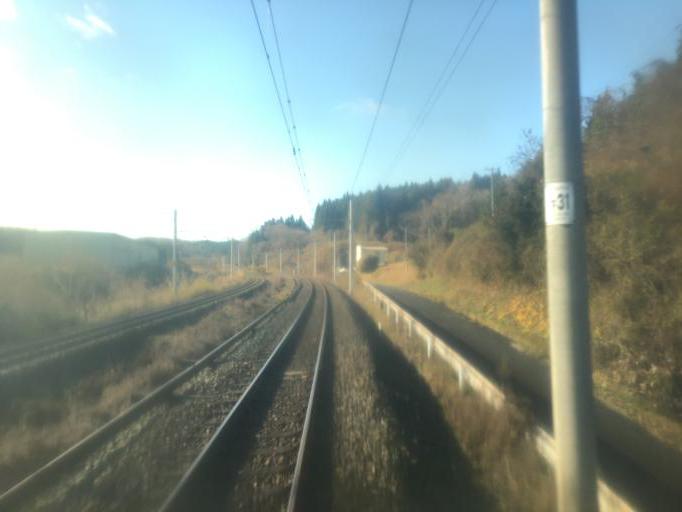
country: JP
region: Iwate
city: Ichinoseki
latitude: 38.8953
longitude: 141.1234
